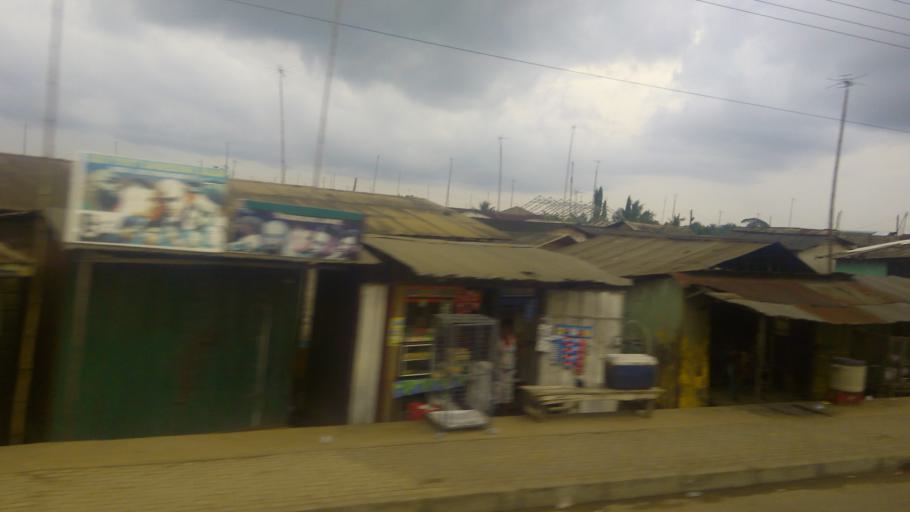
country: GH
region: Western
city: Takoradi
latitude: 4.8945
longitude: -1.9391
